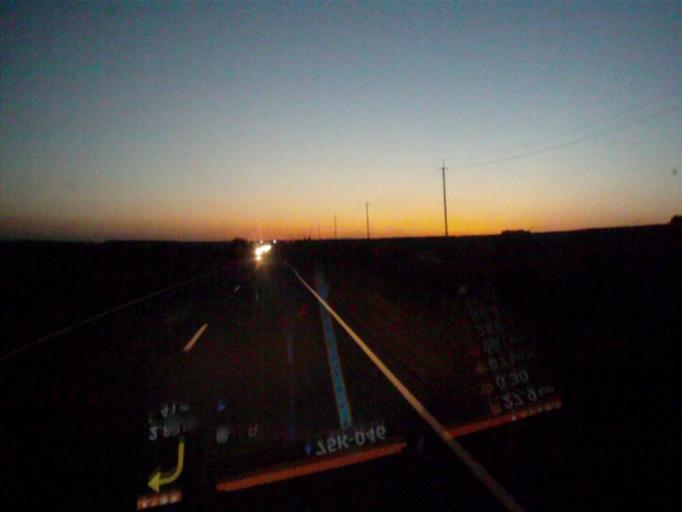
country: RU
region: Chelyabinsk
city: Chebarkul'
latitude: 55.2215
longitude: 60.4930
